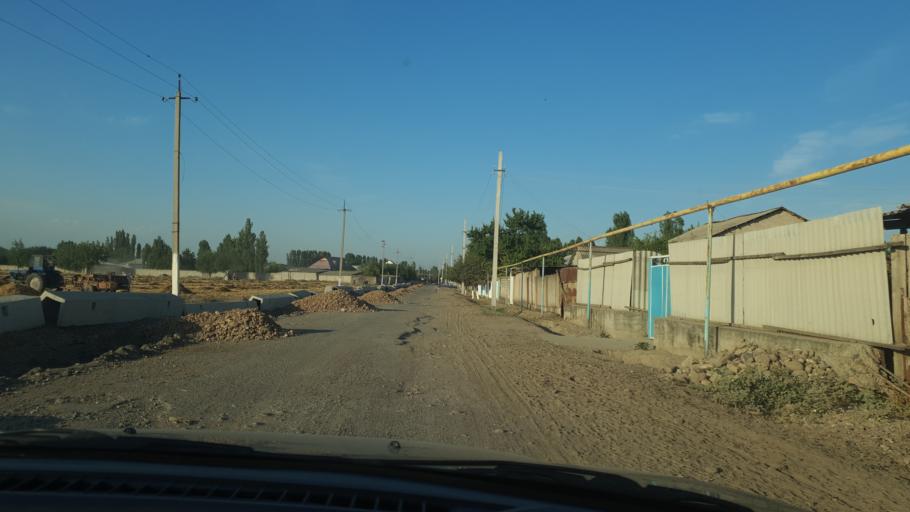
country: UZ
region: Toshkent
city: Tuytepa
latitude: 41.1030
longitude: 69.3868
